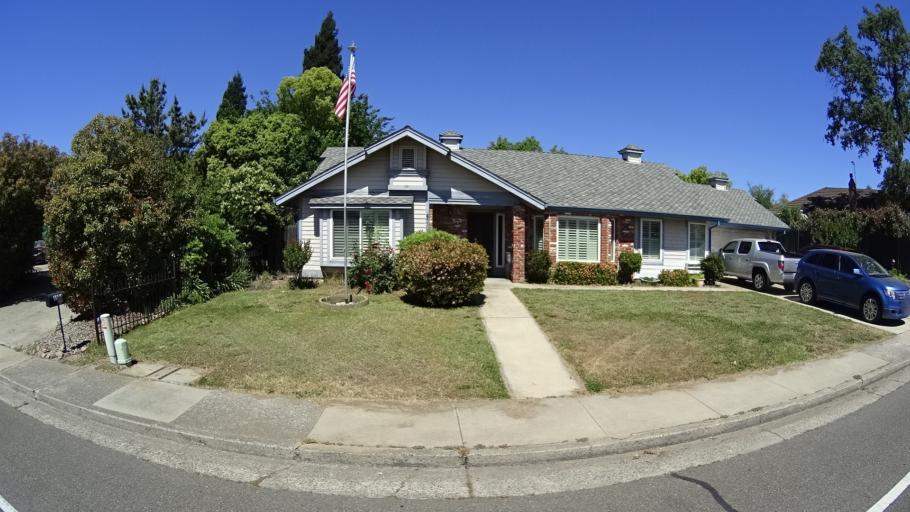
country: US
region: California
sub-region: Placer County
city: Rocklin
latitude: 38.7931
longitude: -121.2203
